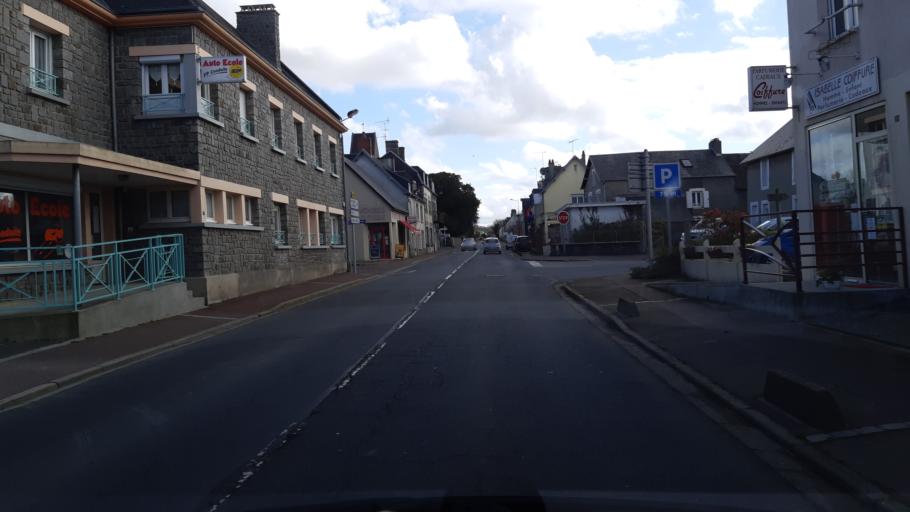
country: FR
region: Lower Normandy
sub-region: Departement de la Manche
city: Agneaux
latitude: 49.0501
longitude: -1.1287
